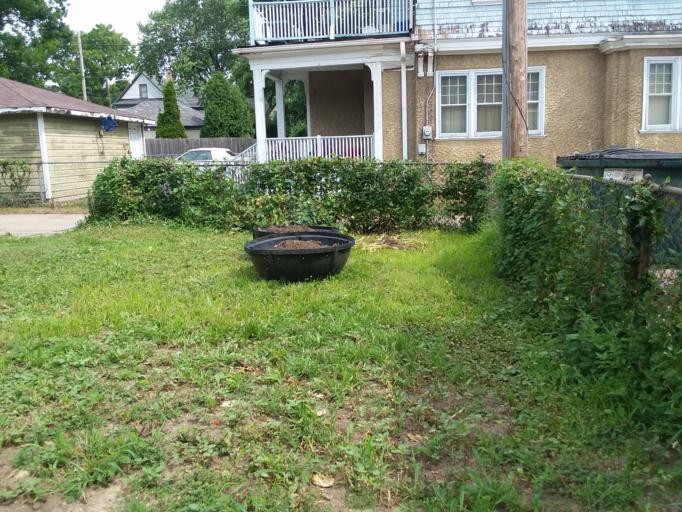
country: US
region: Wisconsin
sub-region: Milwaukee County
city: West Milwaukee
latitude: 43.0408
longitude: -87.9556
